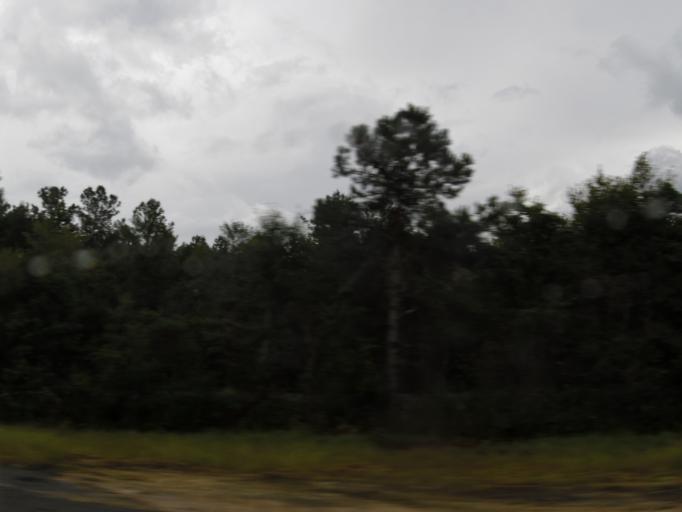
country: US
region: Georgia
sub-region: Wayne County
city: Jesup
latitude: 31.4519
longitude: -81.6993
